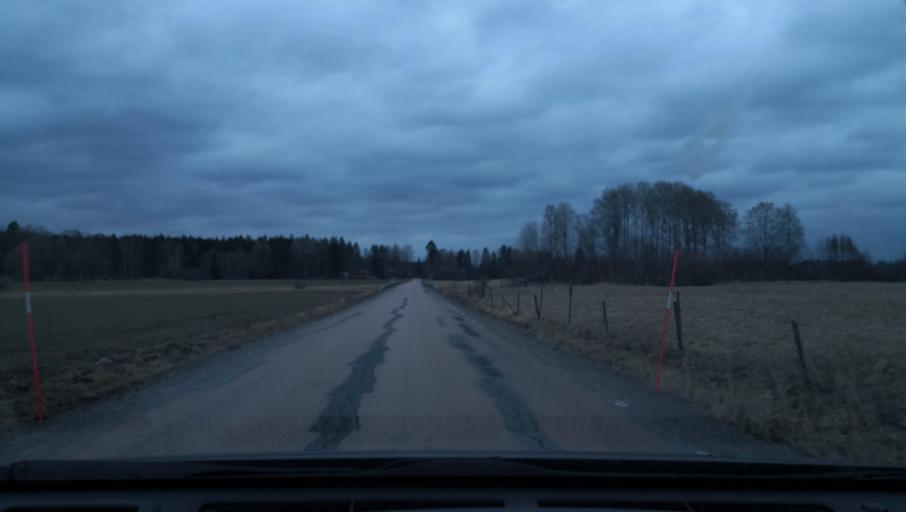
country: SE
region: Vaestmanland
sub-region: Kopings Kommun
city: Kolsva
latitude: 59.5595
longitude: 15.7358
